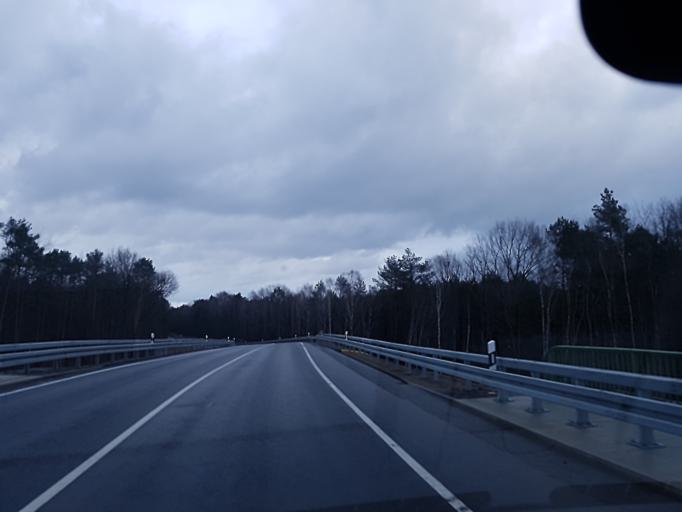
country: DE
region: Brandenburg
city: Hohenleipisch
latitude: 51.5225
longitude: 13.5763
